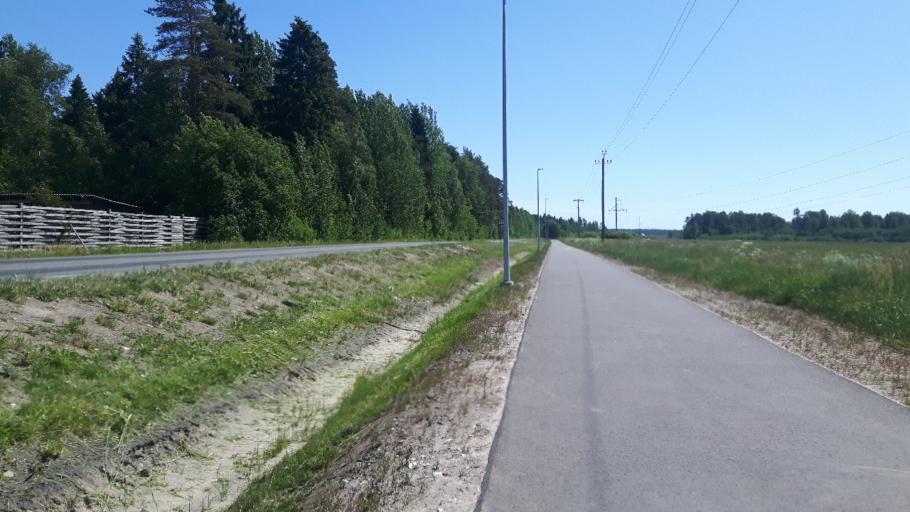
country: EE
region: Raplamaa
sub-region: Kohila vald
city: Kohila
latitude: 59.2119
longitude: 24.6816
